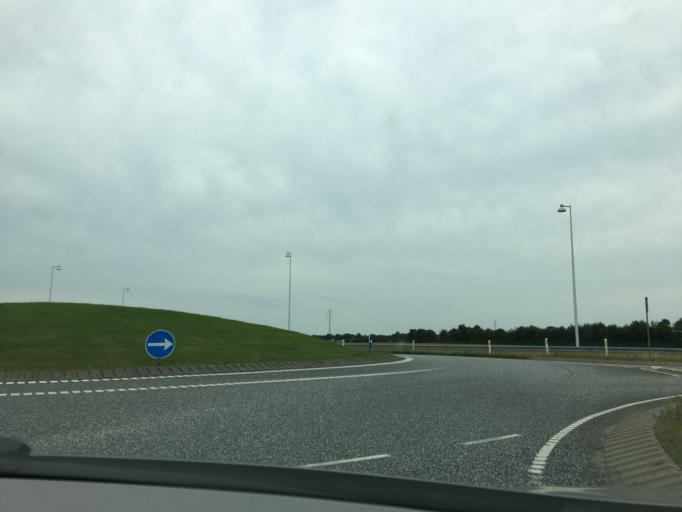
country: DK
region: Central Jutland
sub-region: Herning Kommune
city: Sunds
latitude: 56.2204
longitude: 9.0078
